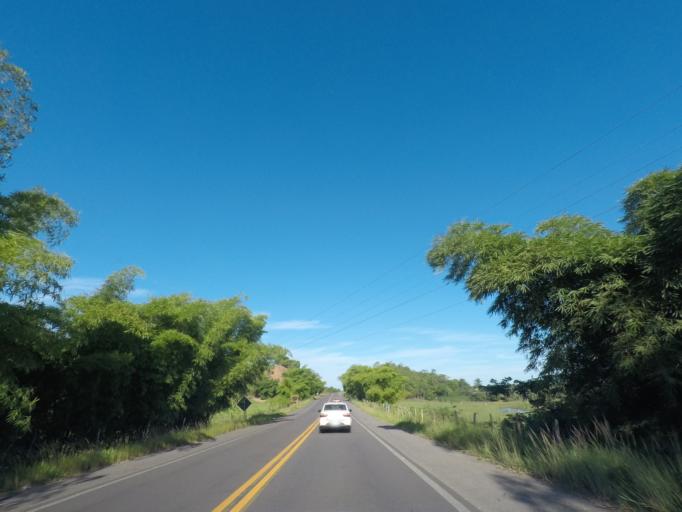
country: BR
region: Bahia
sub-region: Nazare
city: Nazare
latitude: -13.0160
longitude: -38.9807
